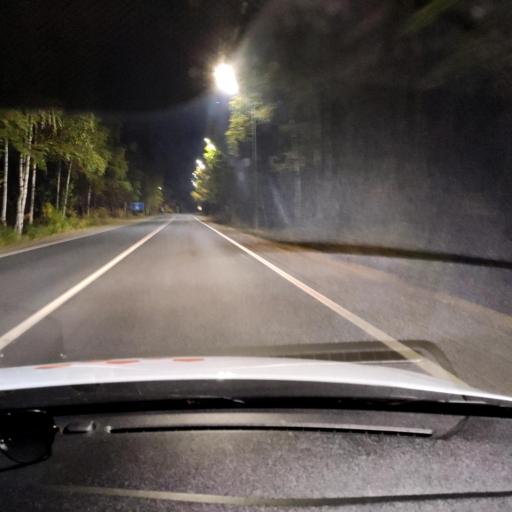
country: RU
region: Tatarstan
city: Verkhniy Uslon
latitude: 55.6379
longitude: 49.0224
